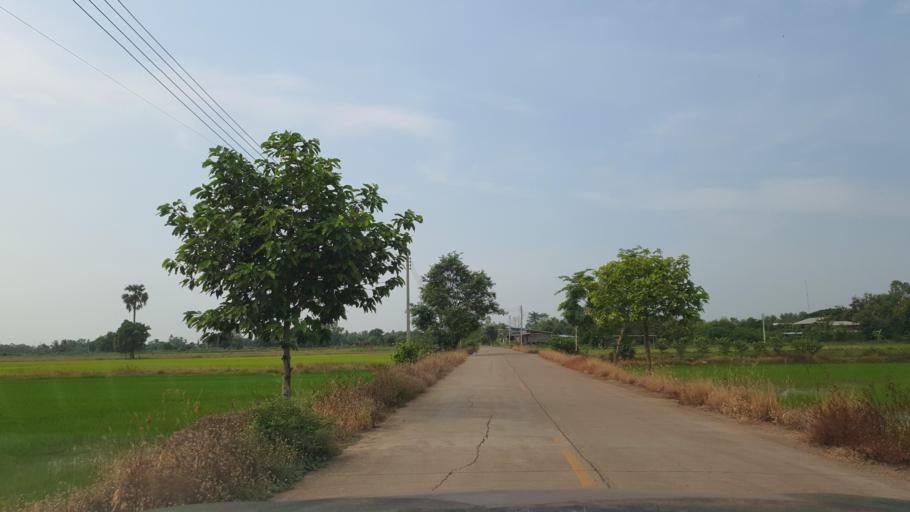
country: TH
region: Phitsanulok
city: Bang Rakam
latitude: 16.8011
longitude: 100.1630
